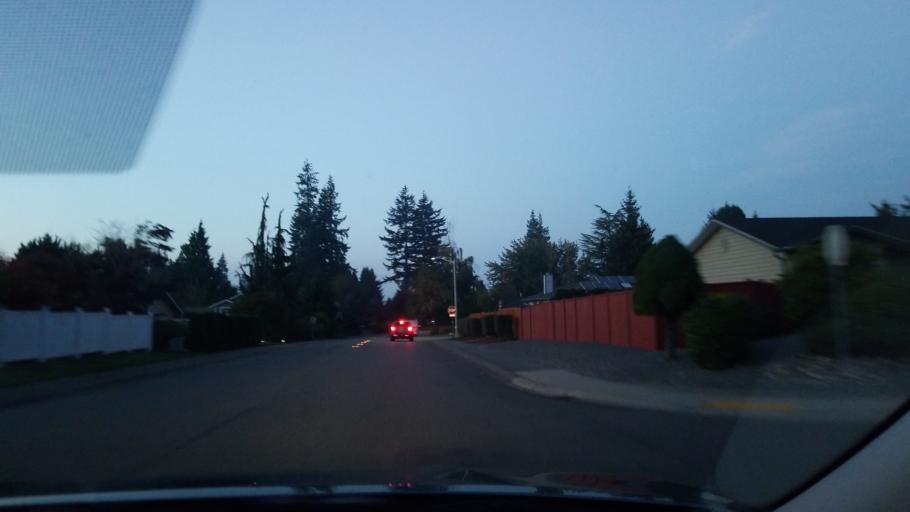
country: US
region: Washington
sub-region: Snohomish County
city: Silver Firs
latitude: 47.8820
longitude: -122.1718
